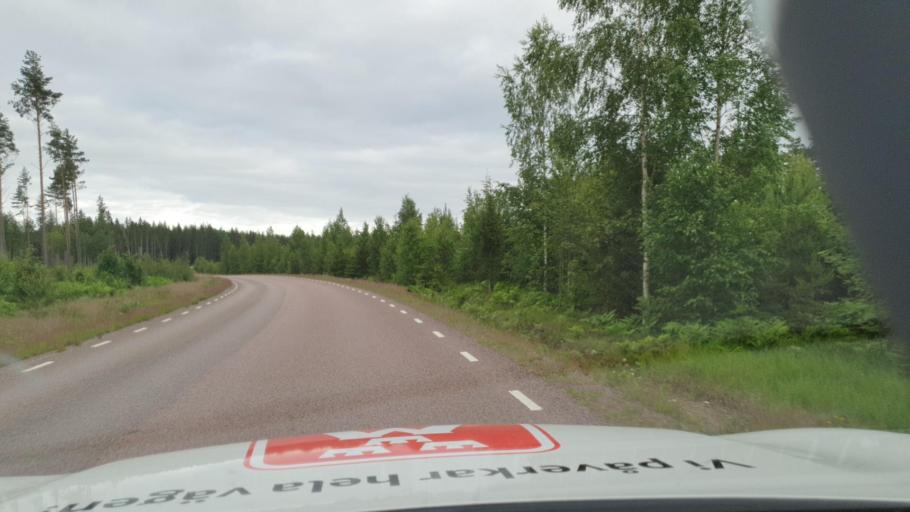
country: SE
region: Vaermland
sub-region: Forshaga Kommun
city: Forshaga
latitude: 59.4944
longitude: 13.4033
